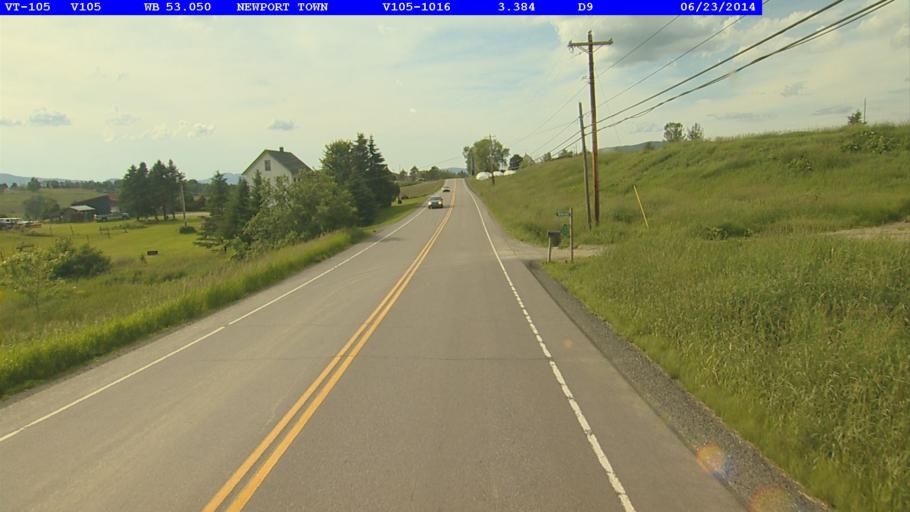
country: US
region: Vermont
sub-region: Orleans County
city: Newport
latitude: 44.9415
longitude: -72.2964
